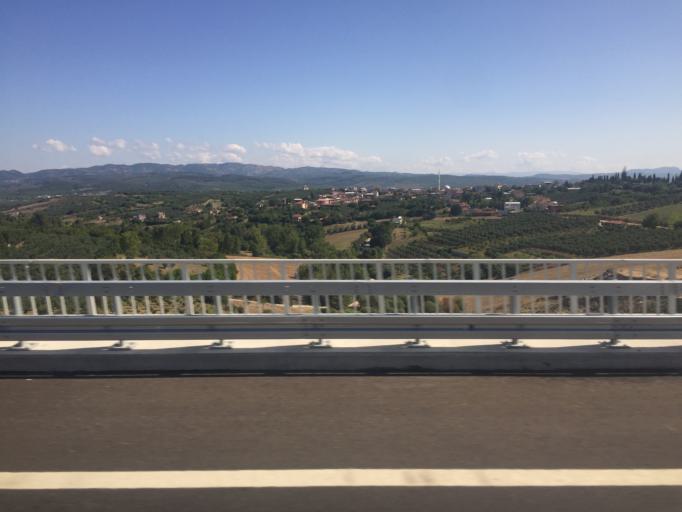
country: TR
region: Bursa
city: Gorukle
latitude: 40.2498
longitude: 28.7502
